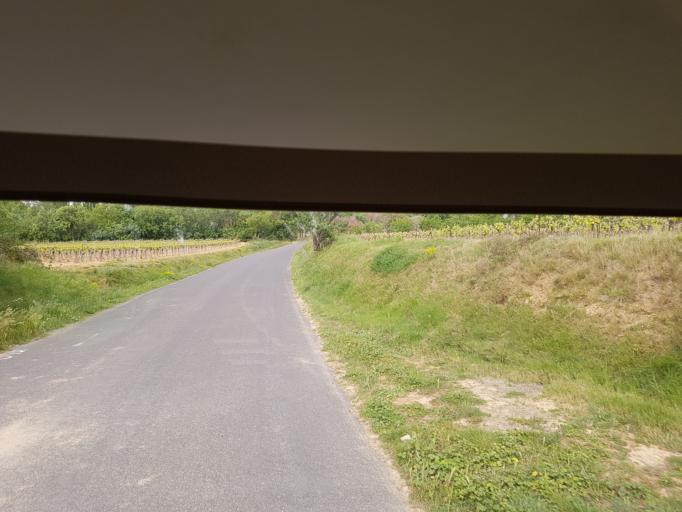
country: FR
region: Languedoc-Roussillon
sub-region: Departement de l'Aude
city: Fleury
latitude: 43.2396
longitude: 3.1466
